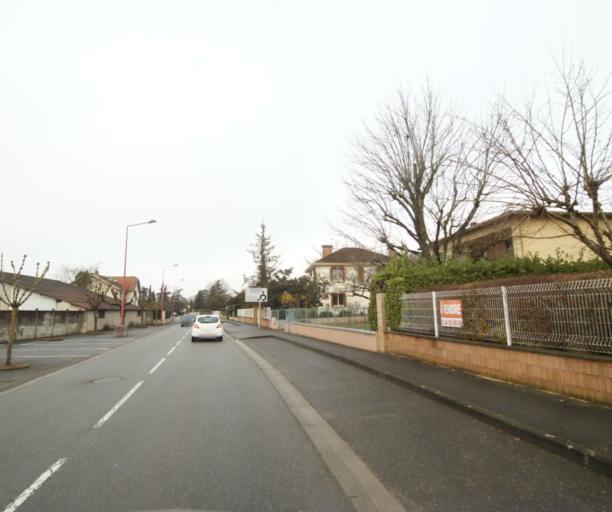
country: FR
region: Midi-Pyrenees
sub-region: Departement de la Haute-Garonne
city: Villemur-sur-Tarn
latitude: 43.8646
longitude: 1.5002
